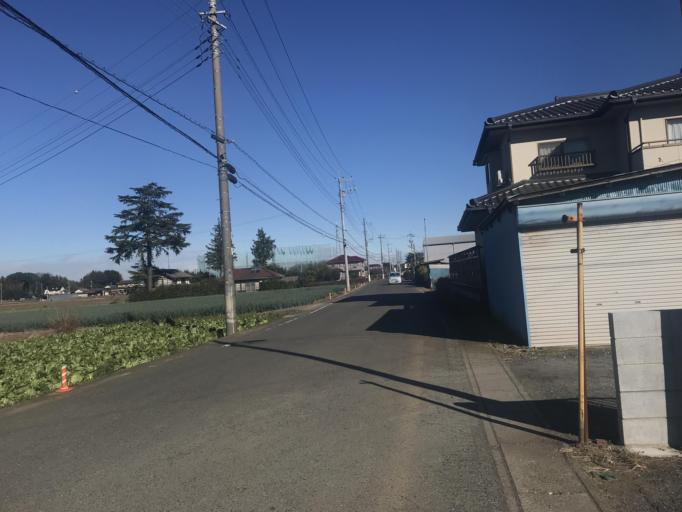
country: JP
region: Ibaraki
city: Yuki
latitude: 36.3170
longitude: 139.8777
